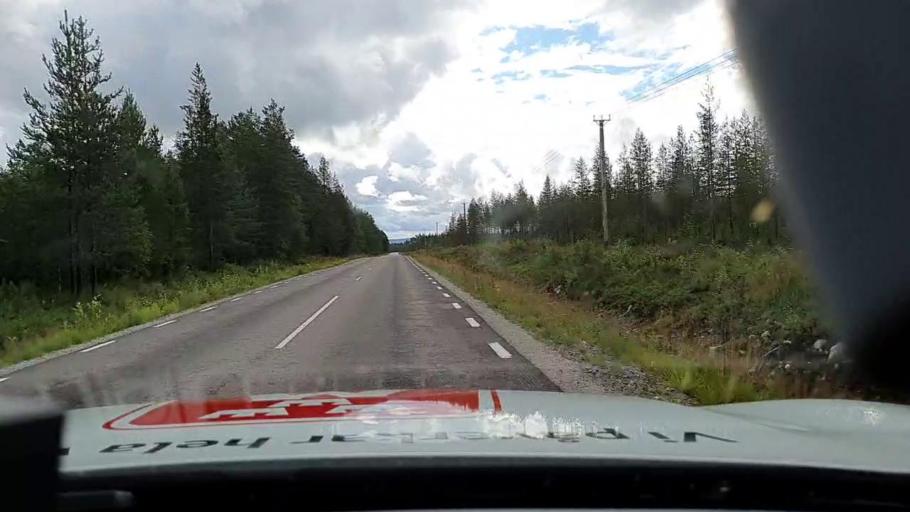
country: SE
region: Norrbotten
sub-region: Overkalix Kommun
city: OEverkalix
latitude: 66.2561
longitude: 22.8621
